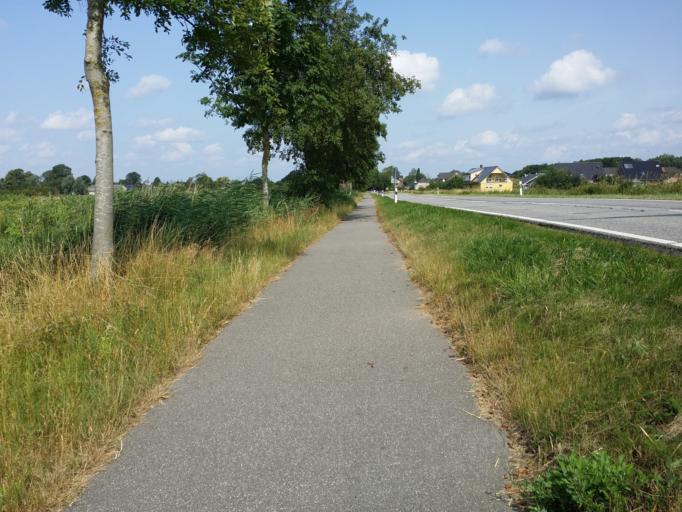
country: DE
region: Schleswig-Holstein
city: Heiligenstedten
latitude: 53.9246
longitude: 9.4742
